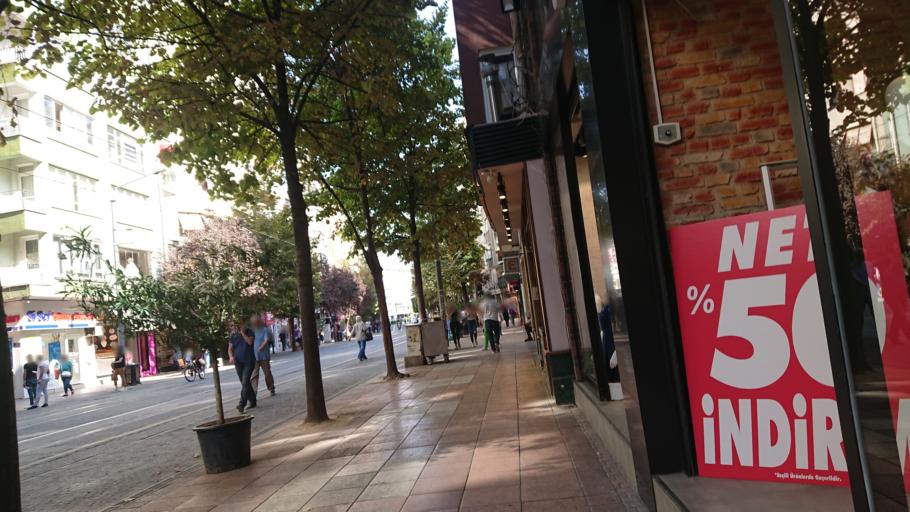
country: TR
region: Eskisehir
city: Eskisehir
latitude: 39.7784
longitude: 30.5155
